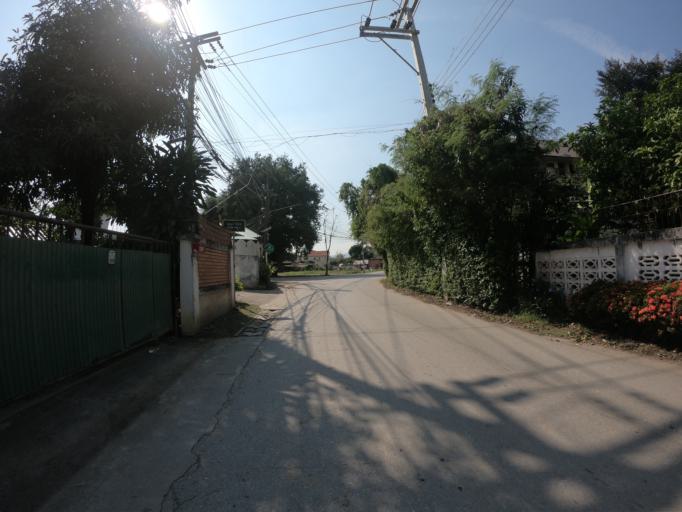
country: TH
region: Chiang Mai
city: Chiang Mai
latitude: 18.8145
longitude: 99.0091
